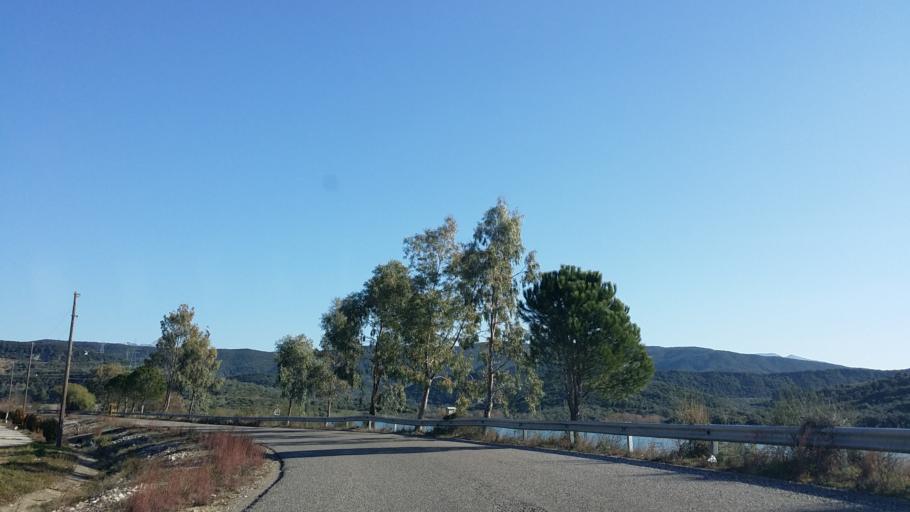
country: GR
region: West Greece
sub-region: Nomos Aitolias kai Akarnanias
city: Lepenou
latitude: 38.7071
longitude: 21.3346
